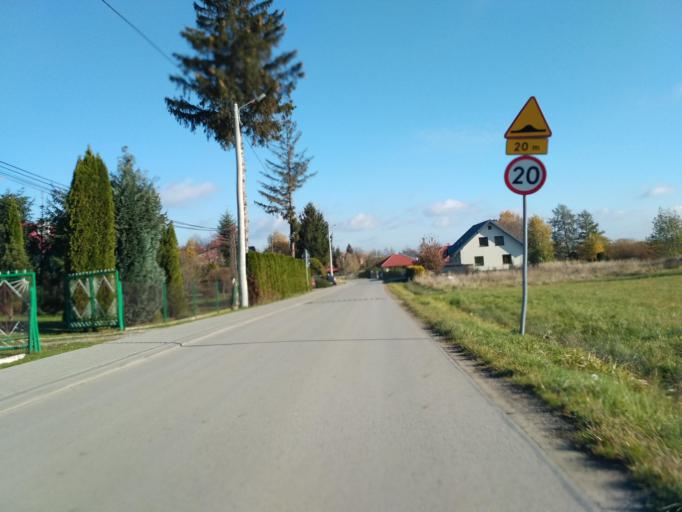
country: PL
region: Subcarpathian Voivodeship
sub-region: Powiat rzeszowski
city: Niechobrz
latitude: 49.9913
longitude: 21.8666
